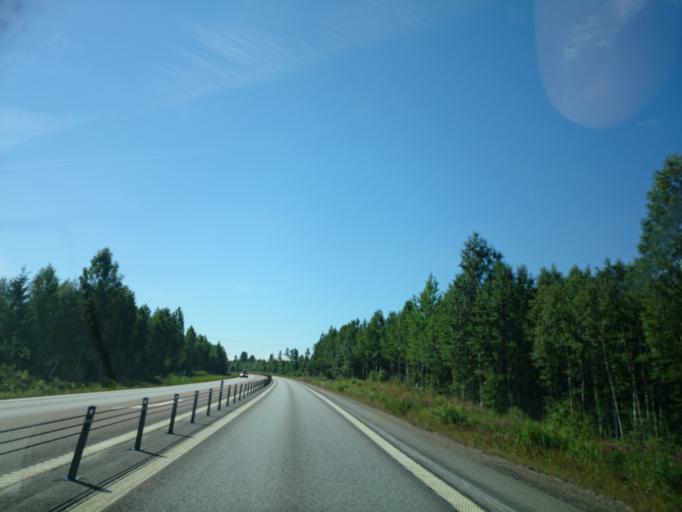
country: SE
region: Gaevleborg
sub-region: Gavle Kommun
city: Gavle
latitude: 60.7753
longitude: 17.0714
